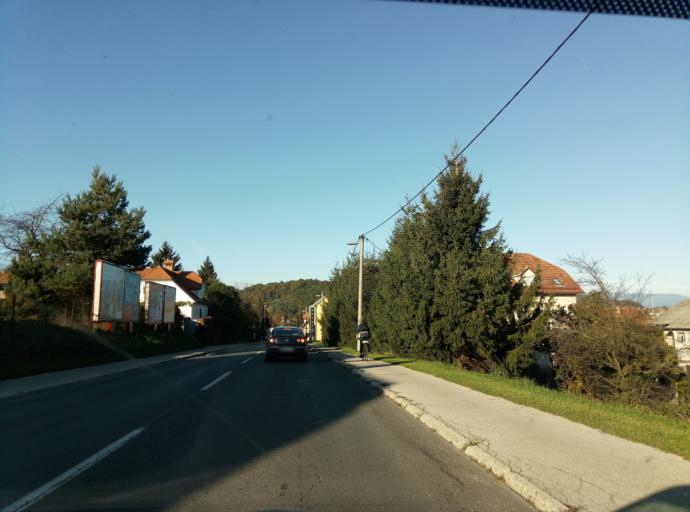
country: SI
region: Ljubljana
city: Ljubljana
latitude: 46.0927
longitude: 14.5149
